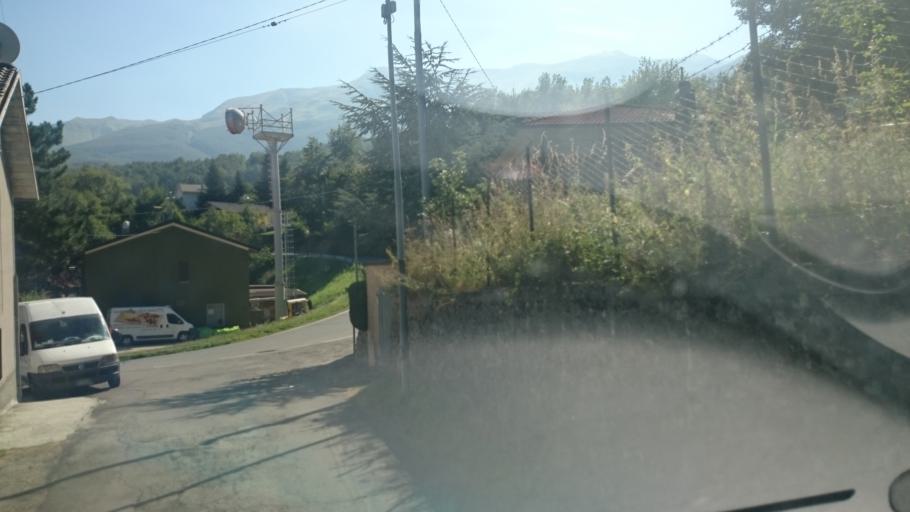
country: IT
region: Emilia-Romagna
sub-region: Provincia di Reggio Emilia
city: Villa Minozzo
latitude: 44.3063
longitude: 10.4327
